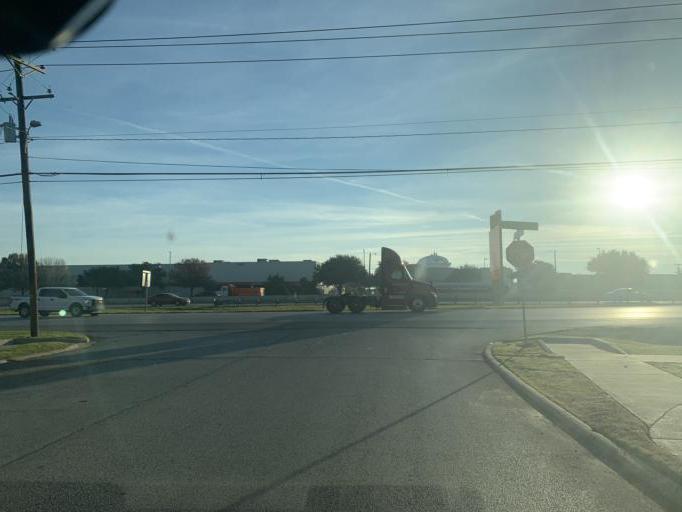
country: US
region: Texas
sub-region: Tarrant County
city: Euless
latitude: 32.7897
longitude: -97.0589
